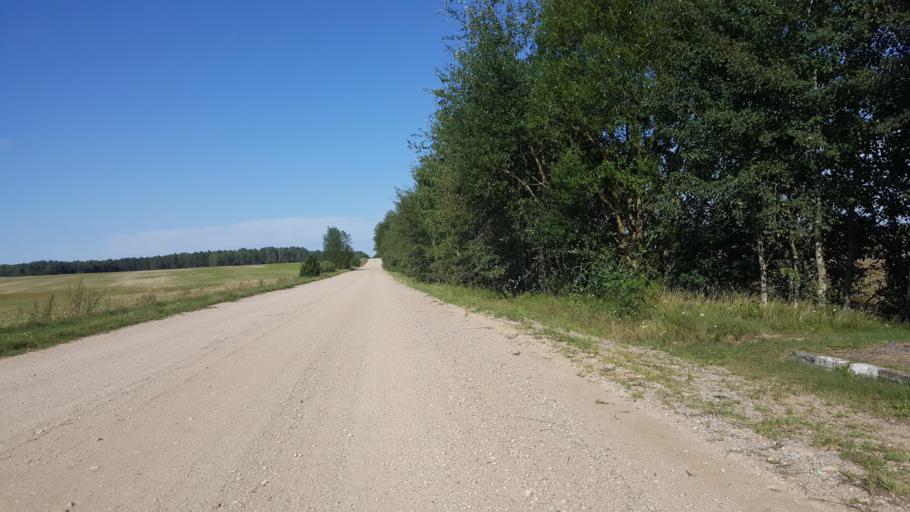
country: BY
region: Brest
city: Kamyanyets
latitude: 52.3583
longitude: 23.7002
